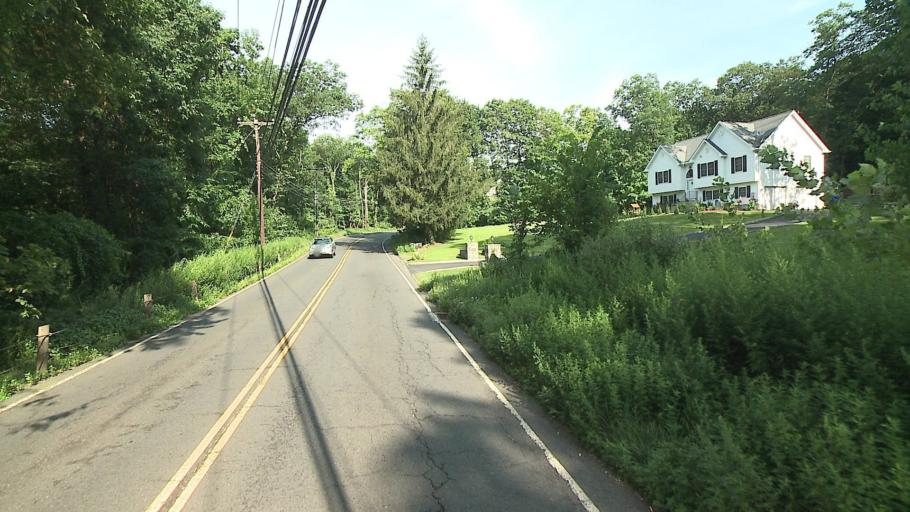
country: US
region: Connecticut
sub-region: Fairfield County
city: Danbury
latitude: 41.4233
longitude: -73.4710
